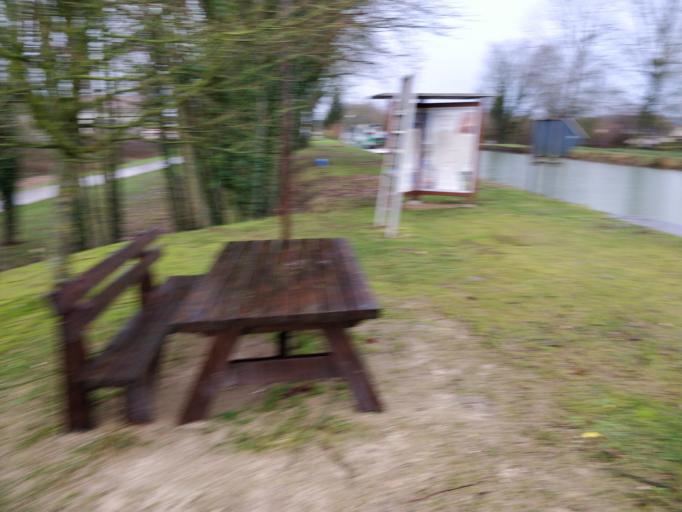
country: FR
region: Champagne-Ardenne
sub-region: Departement de la Marne
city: Pargny-sur-Saulx
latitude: 48.6661
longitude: 4.7337
